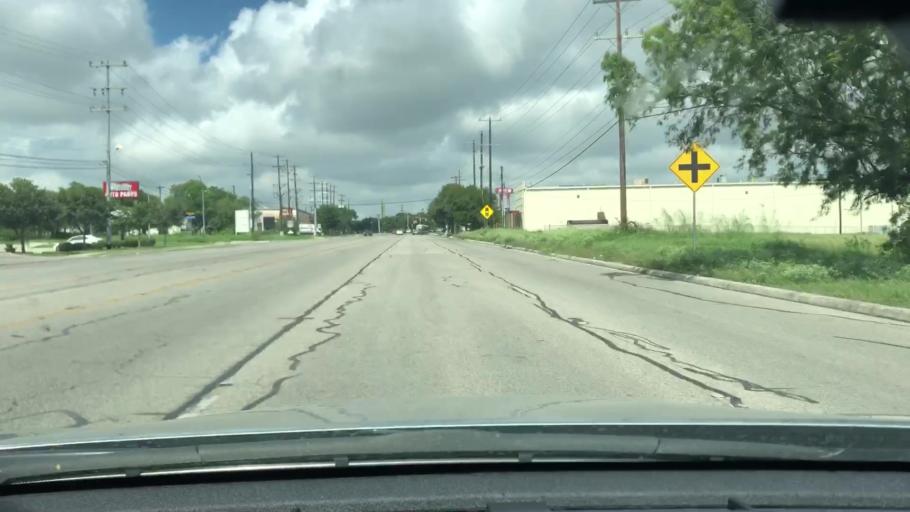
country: US
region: Texas
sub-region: Bexar County
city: Windcrest
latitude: 29.5075
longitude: -98.3694
